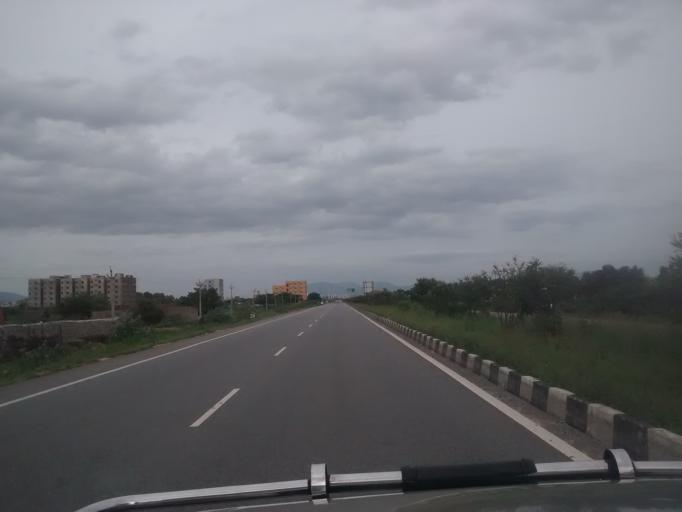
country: IN
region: Andhra Pradesh
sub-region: Chittoor
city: Tirupati
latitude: 13.6045
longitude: 79.3901
